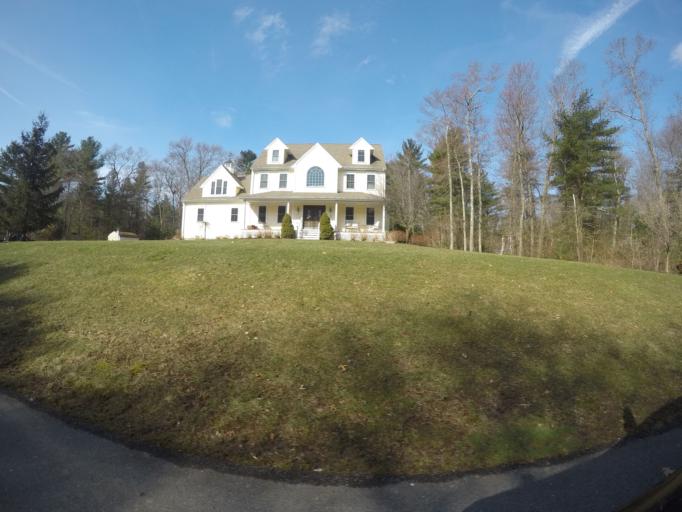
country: US
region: Massachusetts
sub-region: Bristol County
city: Easton
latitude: 42.0196
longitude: -71.1418
